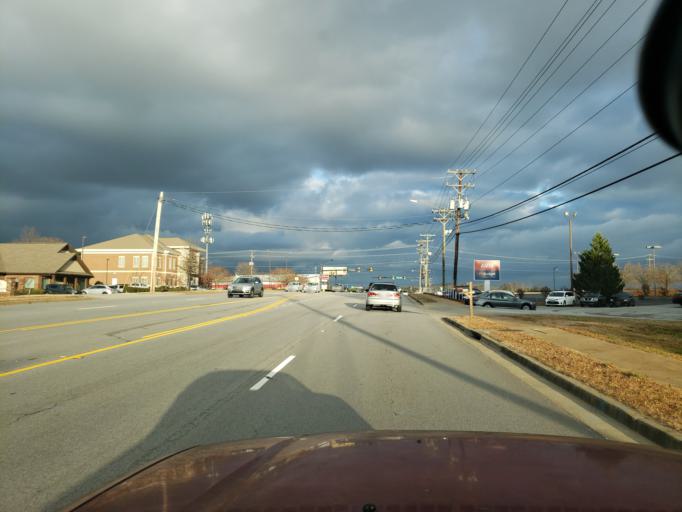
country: US
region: South Carolina
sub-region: Greenville County
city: Greenville
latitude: 34.8354
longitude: -82.3362
